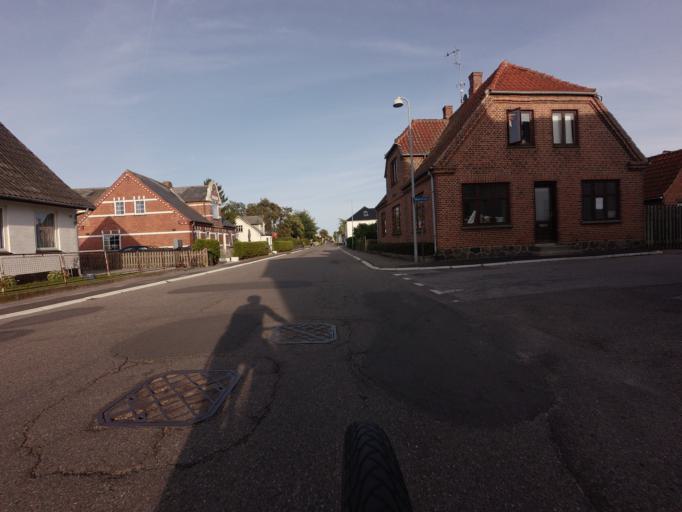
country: DK
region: Zealand
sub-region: Stevns Kommune
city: Store Heddinge
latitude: 55.2562
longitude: 12.3745
